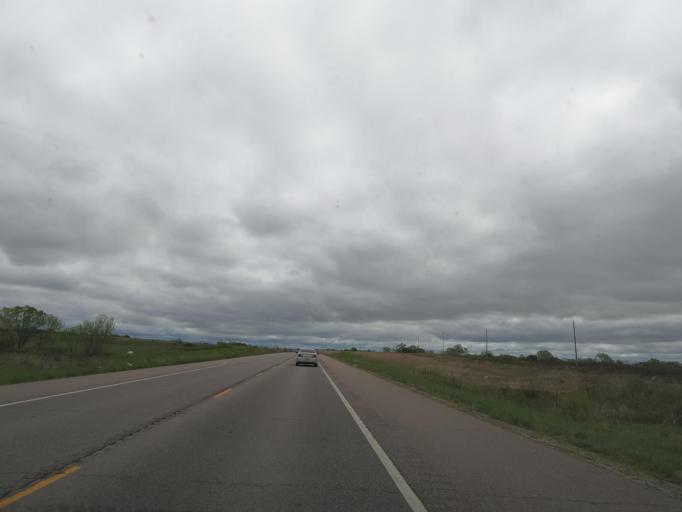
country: US
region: Kansas
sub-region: Elk County
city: Howard
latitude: 37.6360
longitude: -96.2692
